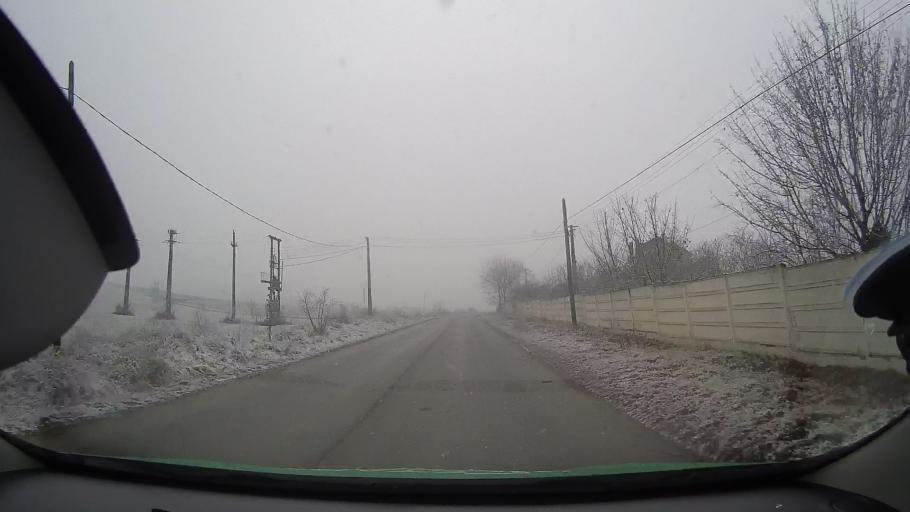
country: RO
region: Alba
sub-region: Comuna Noslac
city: Noslac
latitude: 46.3793
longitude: 23.9006
